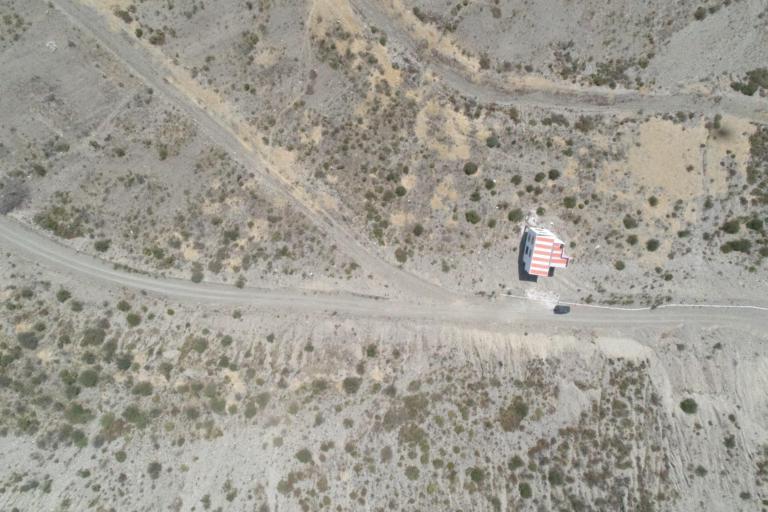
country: BO
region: La Paz
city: La Paz
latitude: -16.4756
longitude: -68.0971
